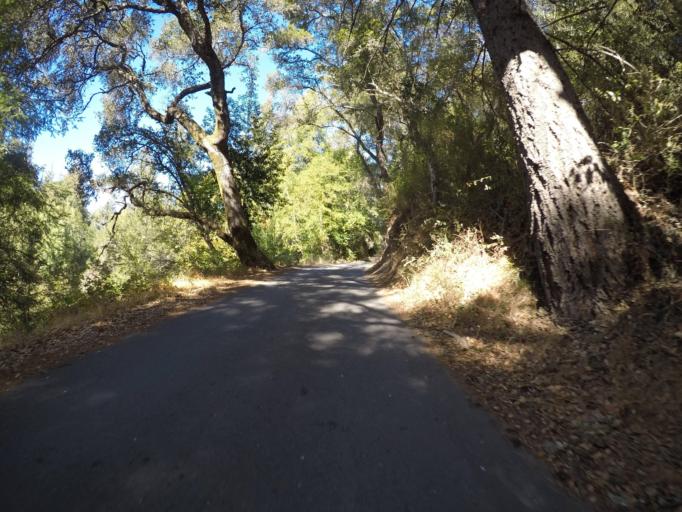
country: US
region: California
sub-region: Santa Cruz County
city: Scotts Valley
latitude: 37.0811
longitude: -121.9962
